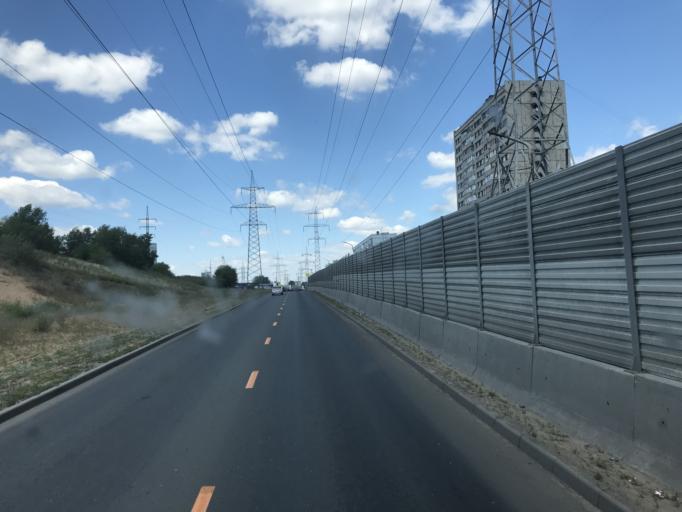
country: RU
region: Samara
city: Zhigulevsk
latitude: 53.4731
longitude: 49.5121
